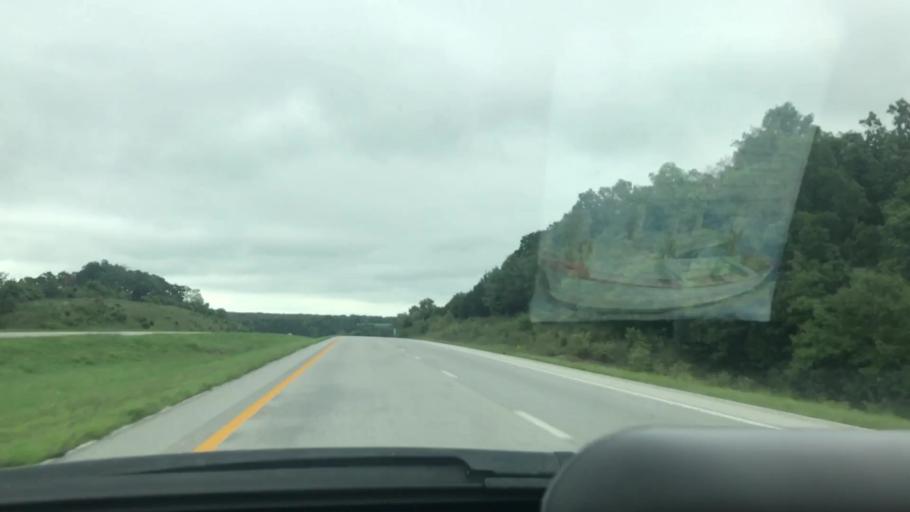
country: US
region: Missouri
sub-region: Greene County
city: Strafford
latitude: 37.2861
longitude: -93.1909
